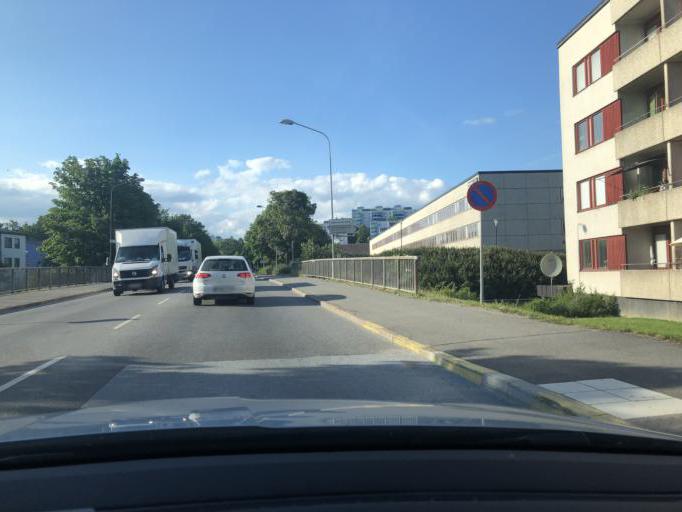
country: SE
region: Stockholm
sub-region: Huddinge Kommun
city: Segeltorp
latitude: 59.2741
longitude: 17.9038
